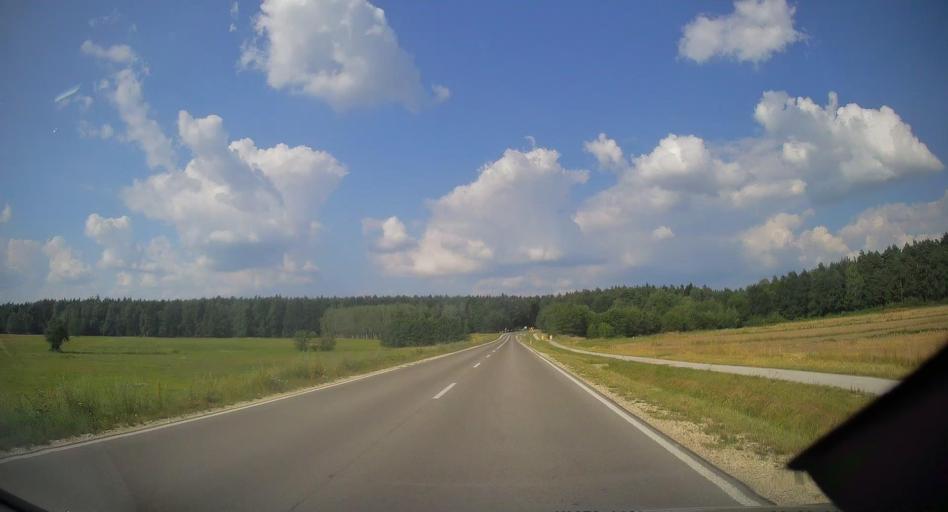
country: PL
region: Swietokrzyskie
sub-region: Powiat kielecki
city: Lopuszno
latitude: 51.0028
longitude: 20.2720
